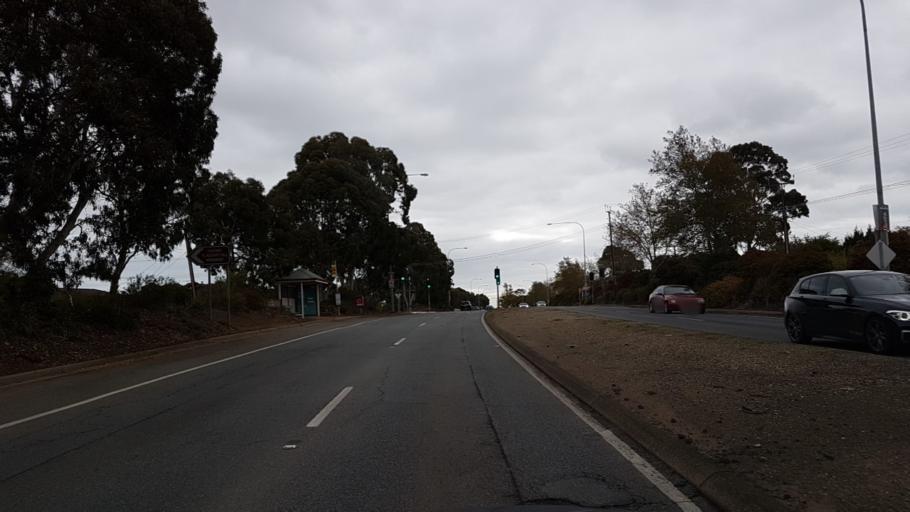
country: AU
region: South Australia
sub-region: Onkaparinga
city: Bedford Park
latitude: -35.0459
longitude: 138.5708
